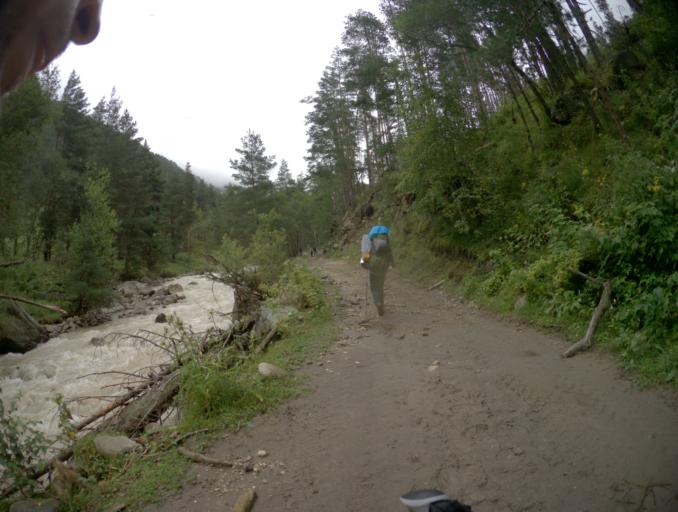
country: RU
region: Karachayevo-Cherkesiya
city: Uchkulan
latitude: 43.4212
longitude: 42.2297
